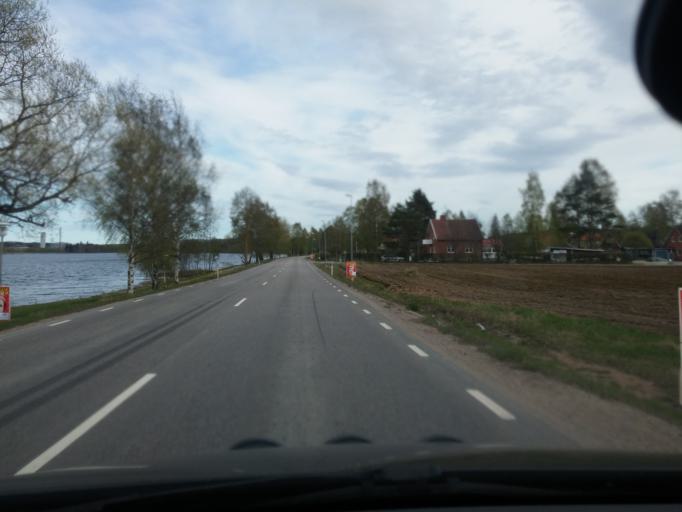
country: SE
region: Gaevleborg
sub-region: Ljusdals Kommun
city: Ljusdal
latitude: 61.8250
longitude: 16.0711
